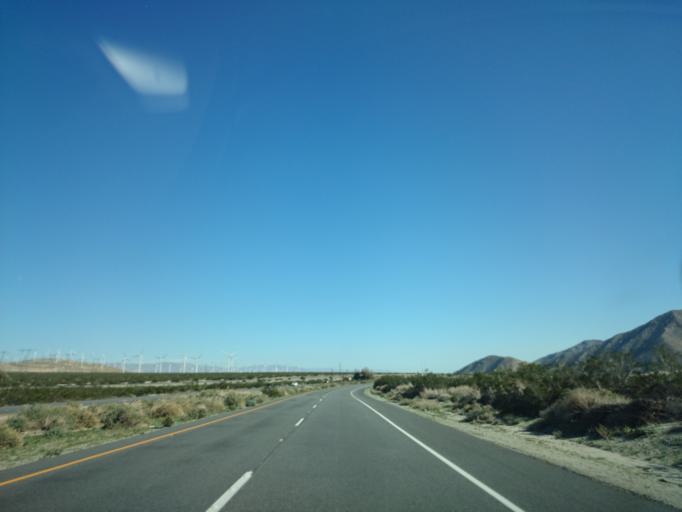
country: US
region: California
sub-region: Riverside County
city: Garnet
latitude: 33.9134
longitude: -116.6639
